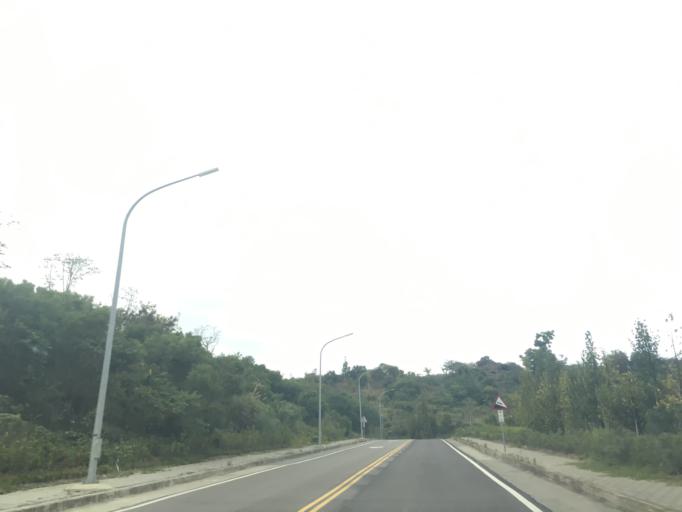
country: TW
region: Taiwan
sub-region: Taichung City
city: Taichung
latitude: 24.1729
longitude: 120.7688
